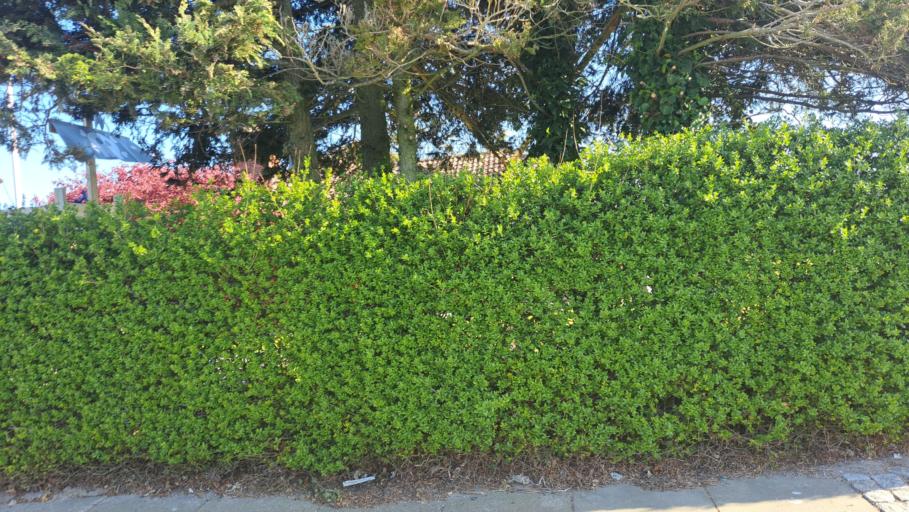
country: DK
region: Central Jutland
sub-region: Hedensted Kommune
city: Hedensted
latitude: 55.7677
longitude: 9.7067
